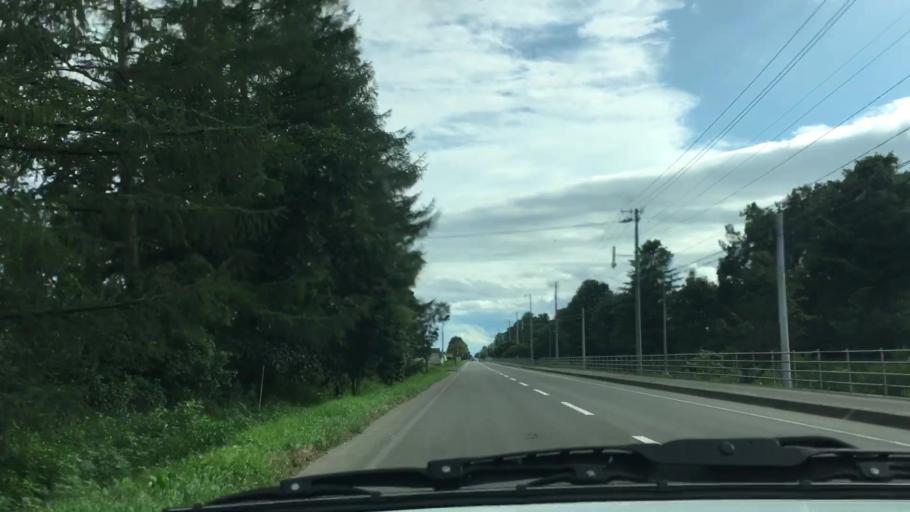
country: JP
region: Hokkaido
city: Otofuke
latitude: 43.2487
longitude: 143.2987
